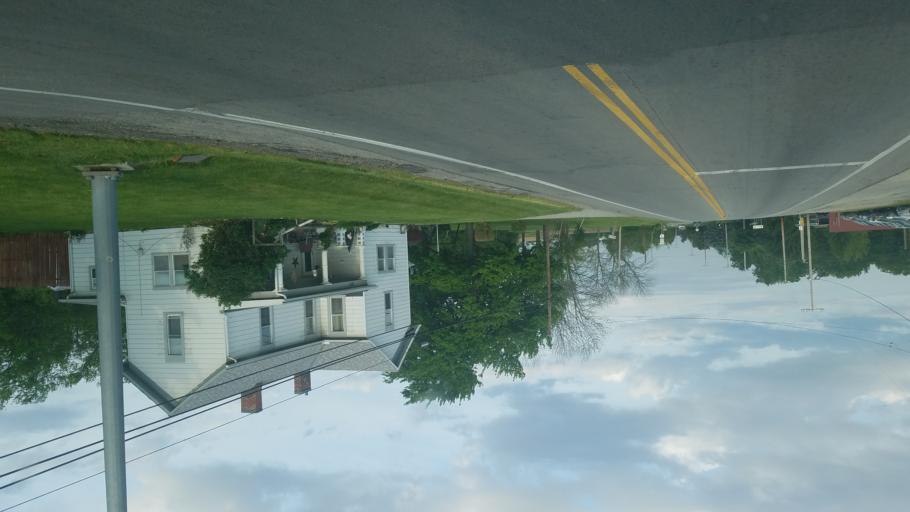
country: US
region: Ohio
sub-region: Clinton County
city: Sabina
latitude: 39.4756
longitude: -83.6726
